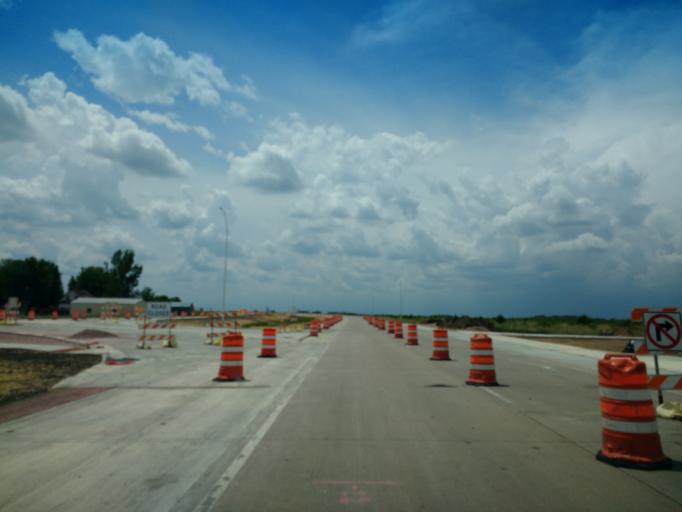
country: US
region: Minnesota
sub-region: Jackson County
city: Lakefield
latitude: 43.7986
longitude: -95.3242
